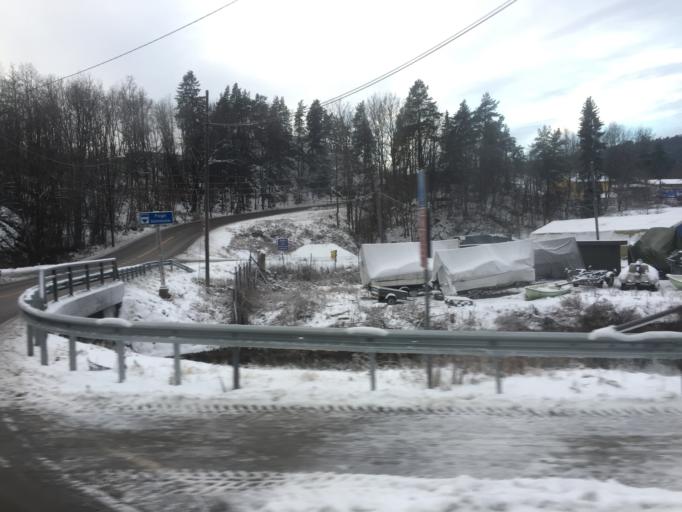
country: NO
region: Akershus
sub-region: As
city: As
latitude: 59.7199
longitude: 10.7289
